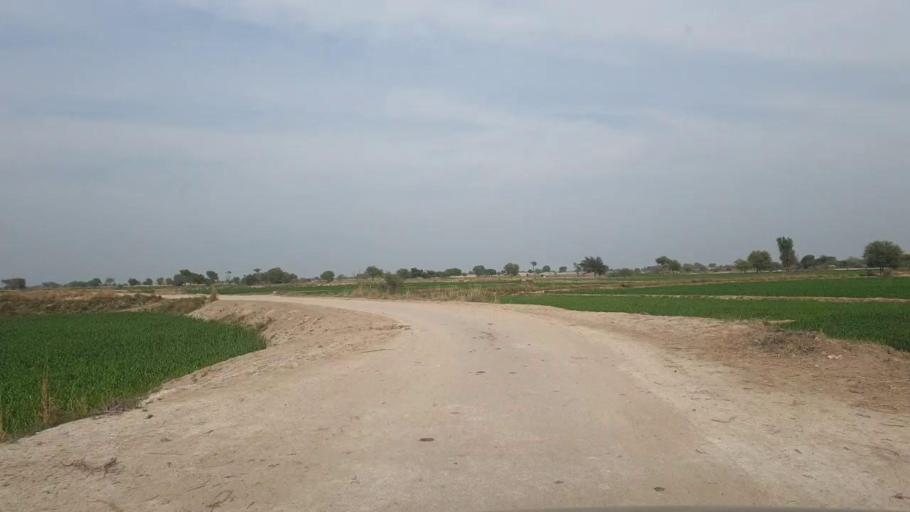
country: PK
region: Sindh
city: Shahpur Chakar
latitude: 26.1133
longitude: 68.5051
